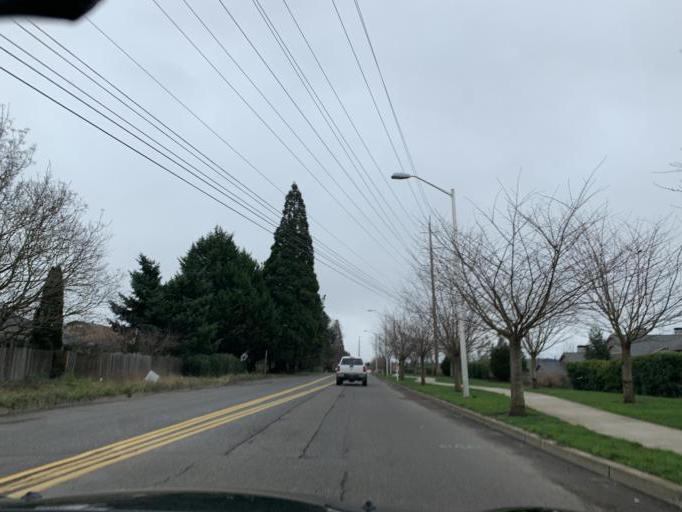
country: US
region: Washington
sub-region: Clark County
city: Mill Plain
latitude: 45.6212
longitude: -122.4925
